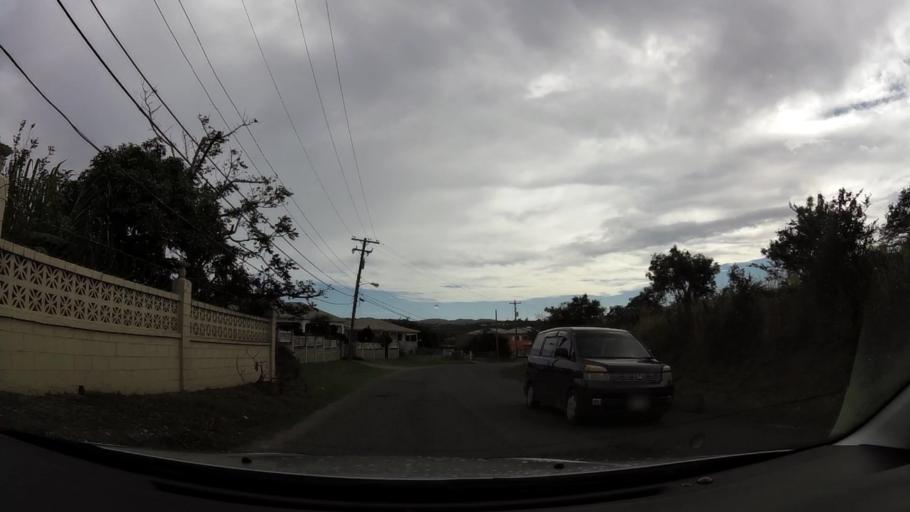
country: AG
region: Saint John
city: Potters Village
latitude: 17.0903
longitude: -61.8132
